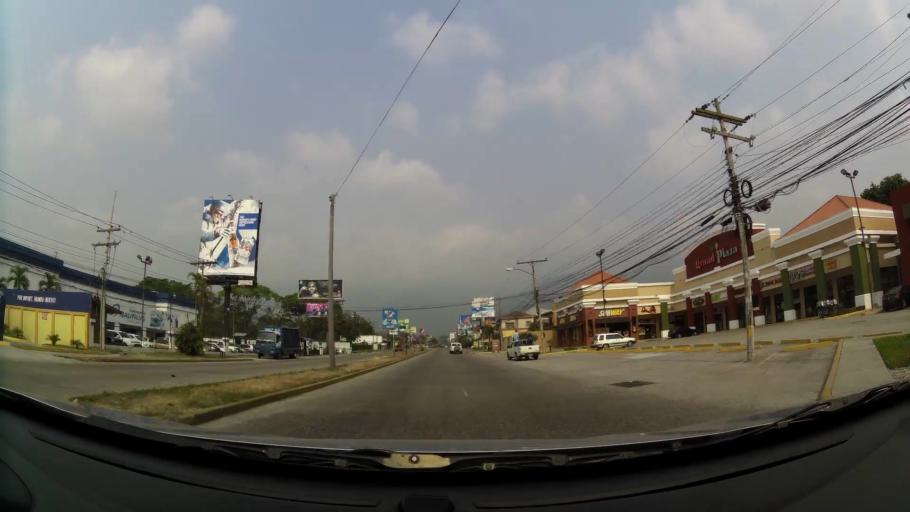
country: HN
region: Cortes
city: San Pedro Sula
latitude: 15.5303
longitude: -88.0234
